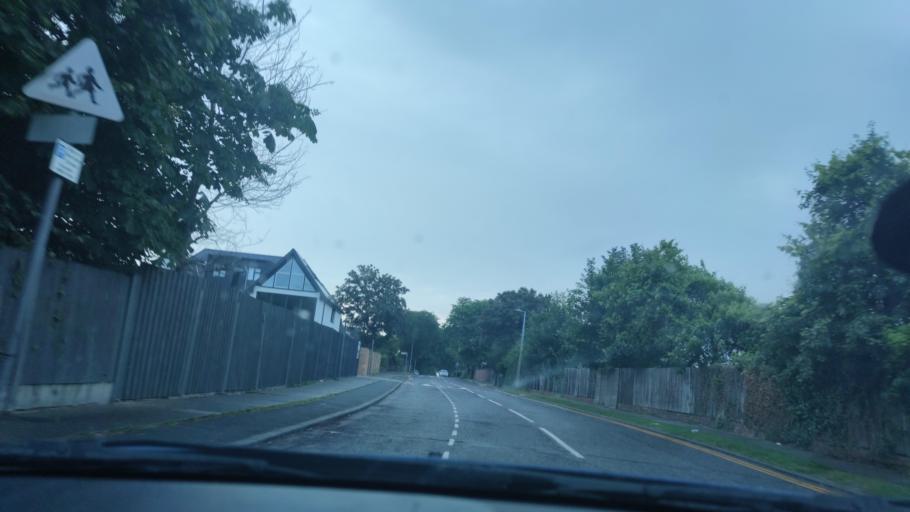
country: GB
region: England
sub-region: Borough of Thurrock
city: Grays
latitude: 51.4826
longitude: 0.3319
